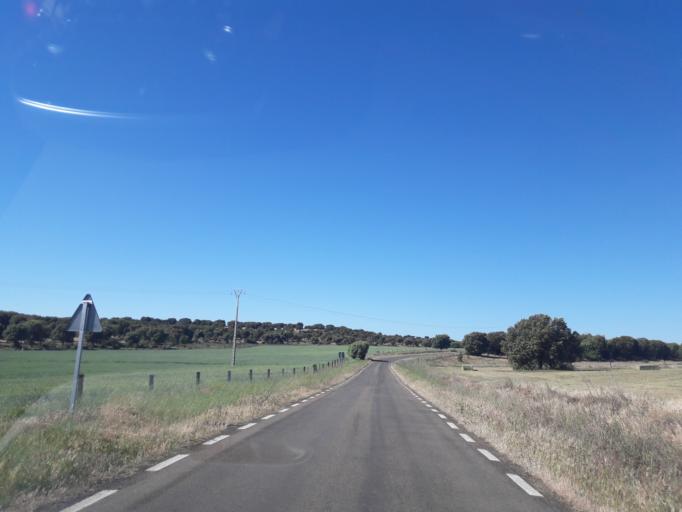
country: ES
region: Castille and Leon
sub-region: Provincia de Salamanca
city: Florida de Liebana
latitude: 41.0054
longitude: -5.7757
